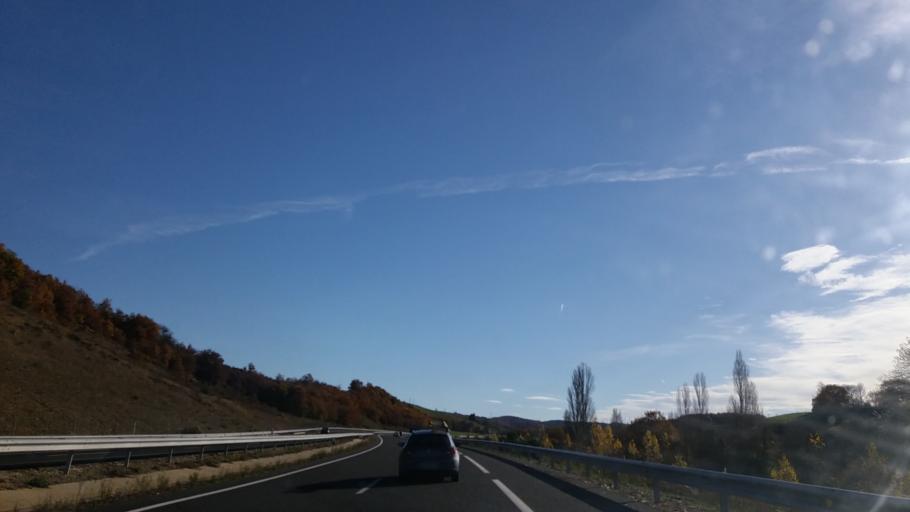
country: ES
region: Navarre
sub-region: Provincia de Navarra
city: Monreal
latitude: 42.6790
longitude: -1.4601
